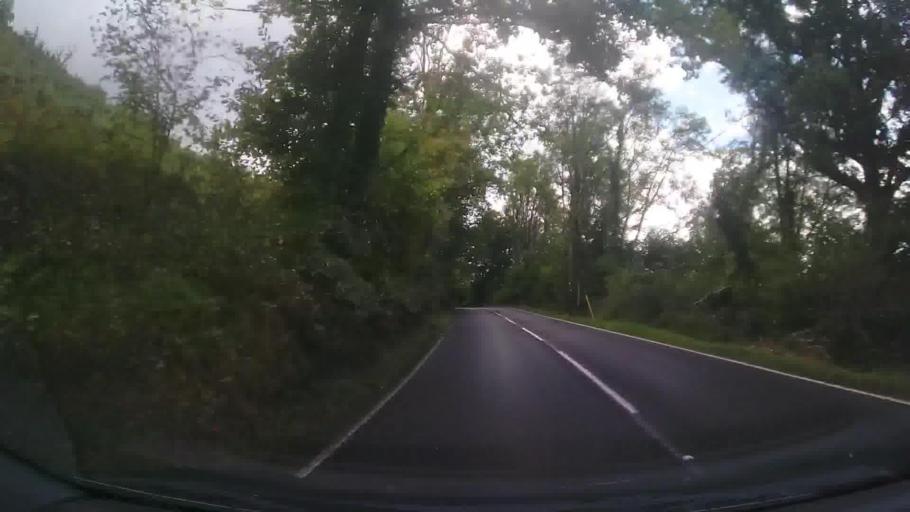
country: GB
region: Wales
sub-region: Carmarthenshire
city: Llandovery
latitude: 52.0514
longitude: -3.7289
